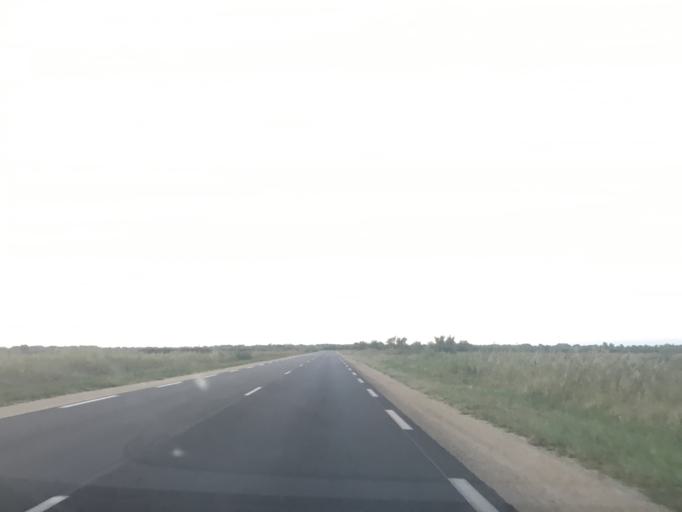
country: FR
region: Provence-Alpes-Cote d'Azur
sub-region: Departement des Bouches-du-Rhone
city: Saintes-Maries-de-la-Mer
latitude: 43.5345
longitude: 4.4004
